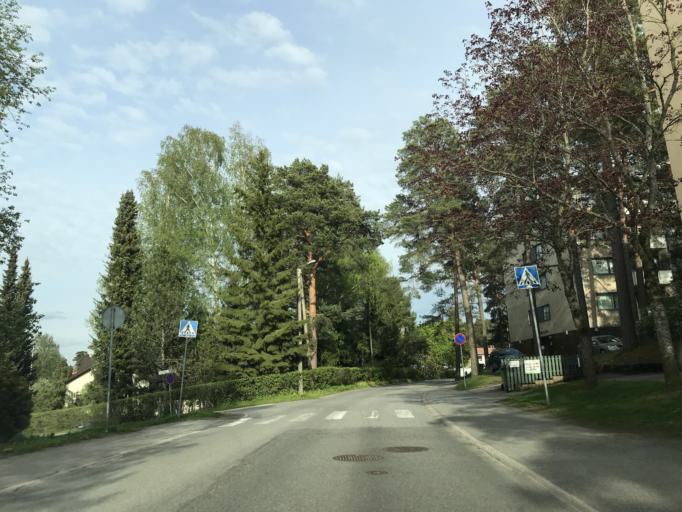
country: FI
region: Varsinais-Suomi
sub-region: Turku
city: Turku
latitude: 60.4376
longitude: 22.3063
